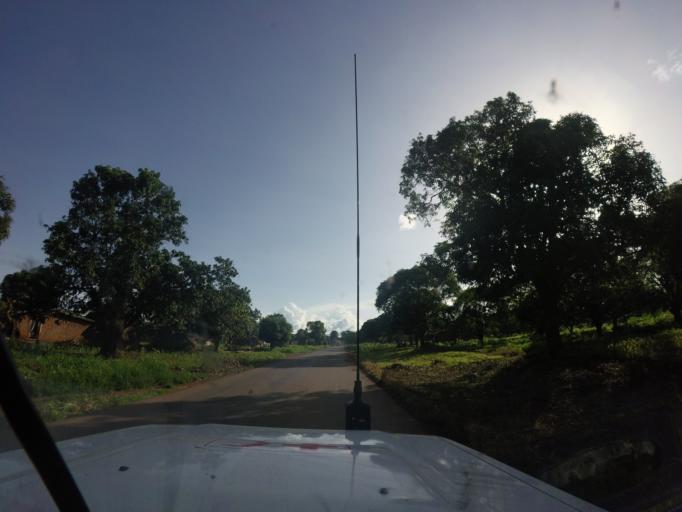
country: GN
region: Kindia
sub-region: Kindia
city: Kindia
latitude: 10.0001
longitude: -12.7075
